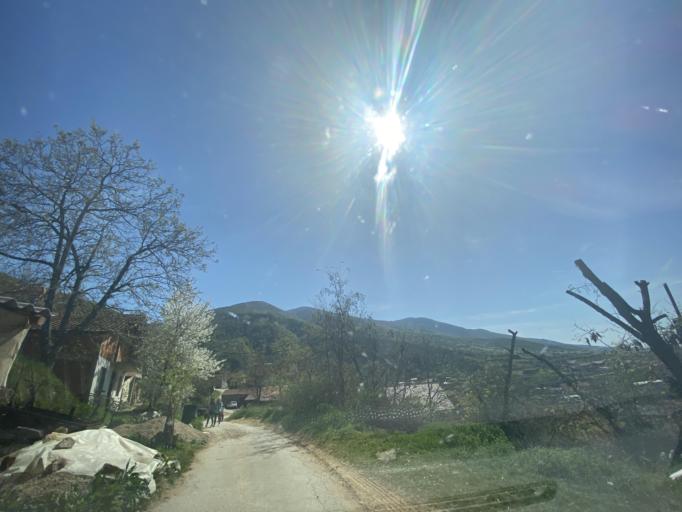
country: MK
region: Zrnovci
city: Zrnovci
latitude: 41.8544
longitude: 22.4480
